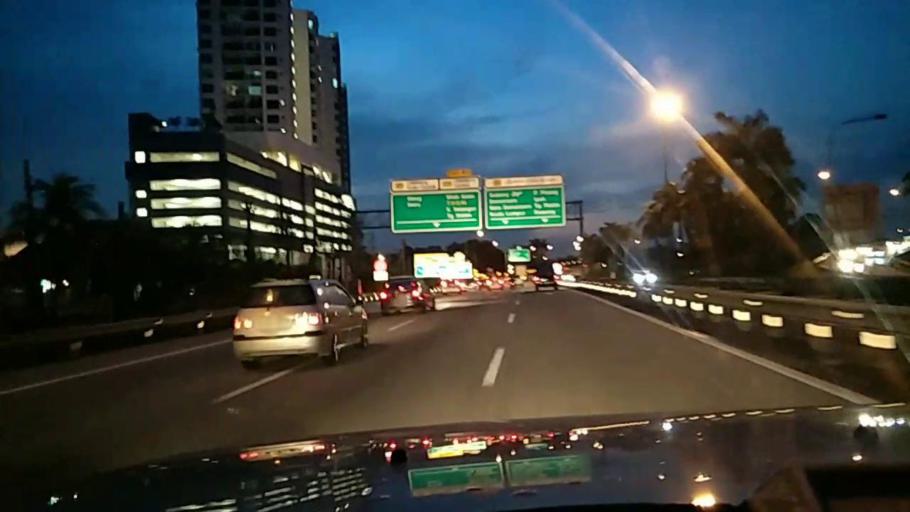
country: MY
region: Selangor
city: Shah Alam
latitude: 3.0886
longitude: 101.5500
